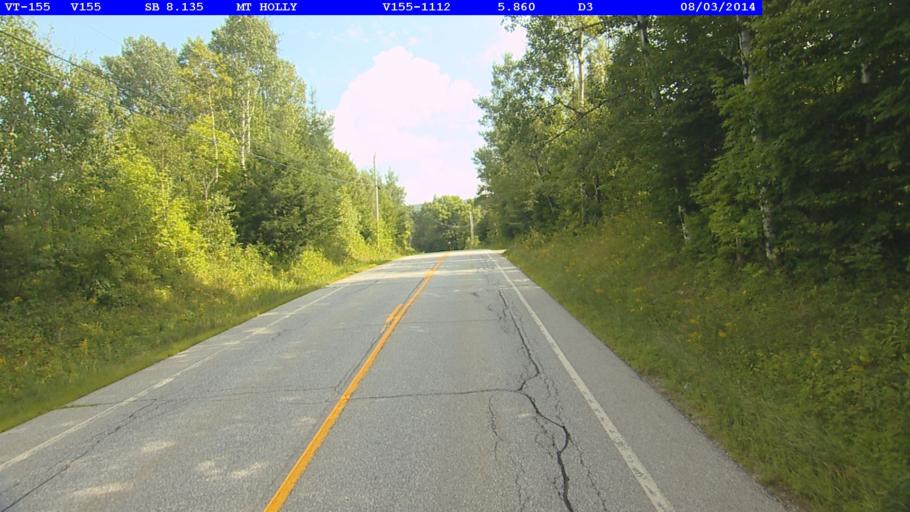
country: US
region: Vermont
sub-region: Rutland County
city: Rutland
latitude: 43.4273
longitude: -72.8575
